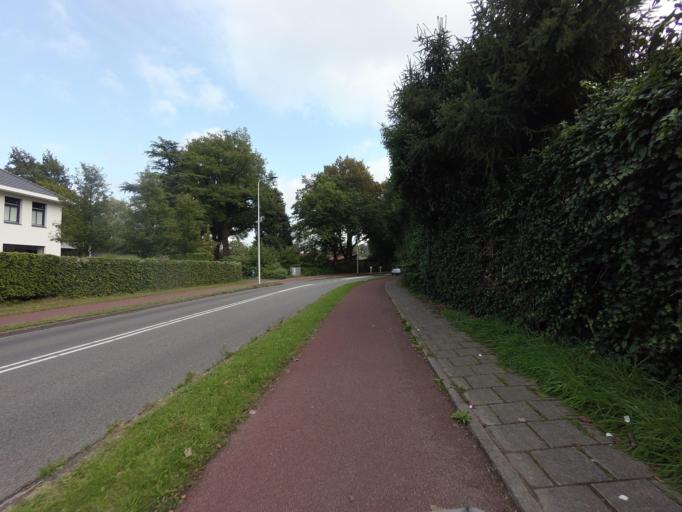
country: NL
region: Overijssel
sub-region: Gemeente Enschede
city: Enschede
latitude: 52.2351
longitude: 6.9212
